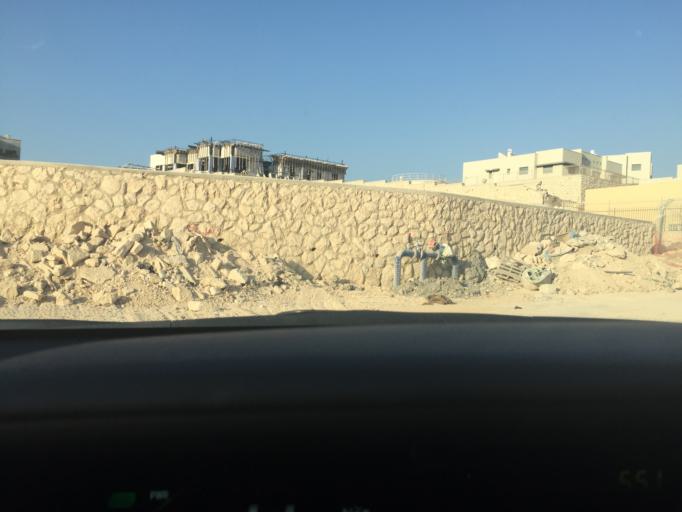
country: PS
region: West Bank
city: Rafat
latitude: 32.0670
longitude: 35.0467
